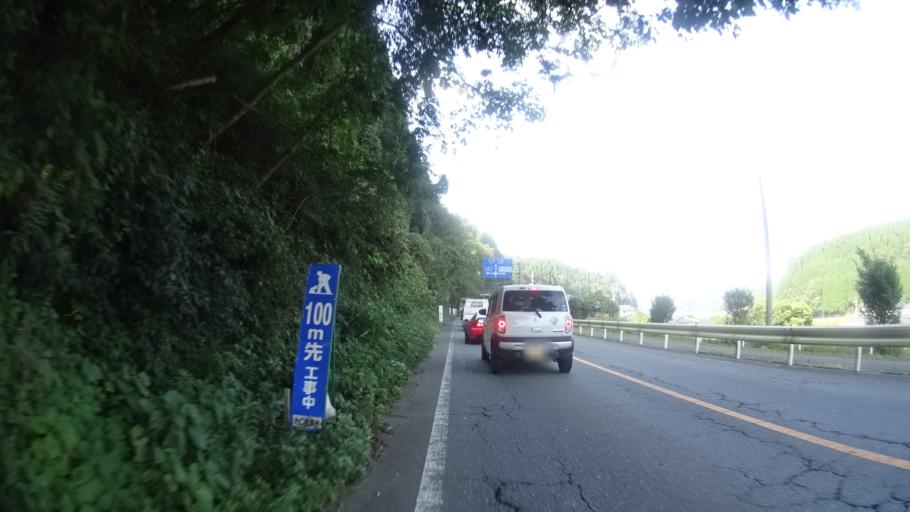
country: JP
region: Kumamoto
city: Aso
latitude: 33.0916
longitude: 131.0669
